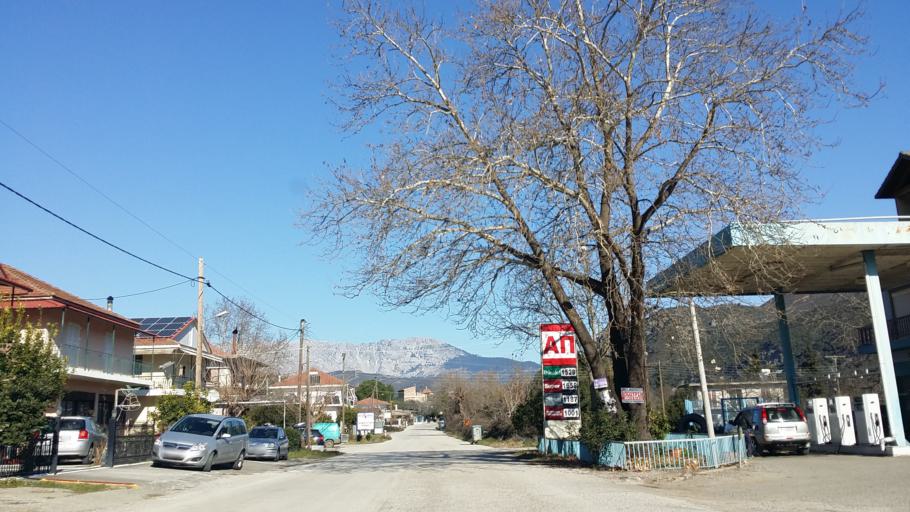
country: GR
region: West Greece
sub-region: Nomos Aitolias kai Akarnanias
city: Sardinia
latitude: 38.8879
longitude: 21.3459
